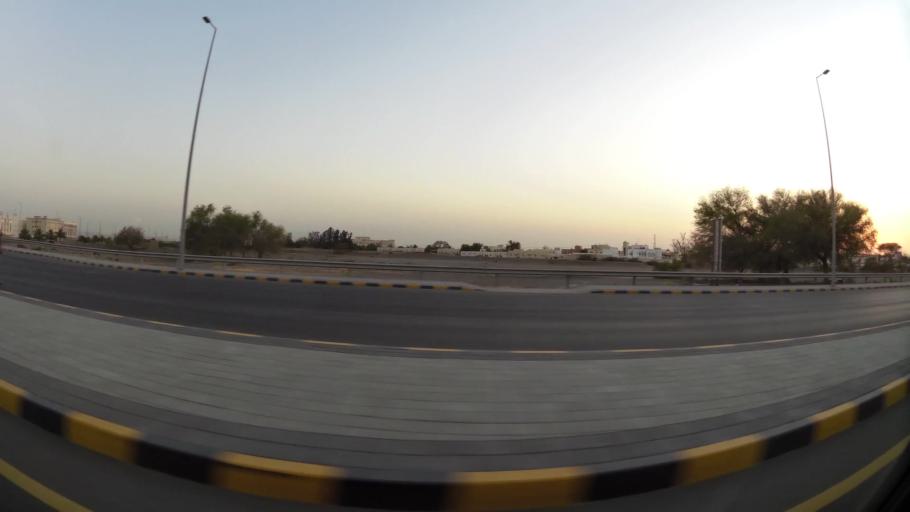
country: OM
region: Muhafazat Masqat
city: As Sib al Jadidah
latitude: 23.6676
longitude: 58.1929
